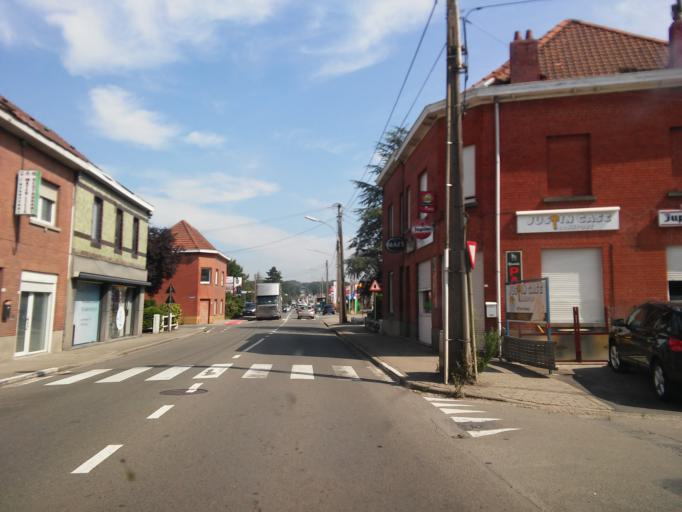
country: BE
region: Flanders
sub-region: Provincie Vlaams-Brabant
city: Ternat
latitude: 50.8756
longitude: 4.1636
